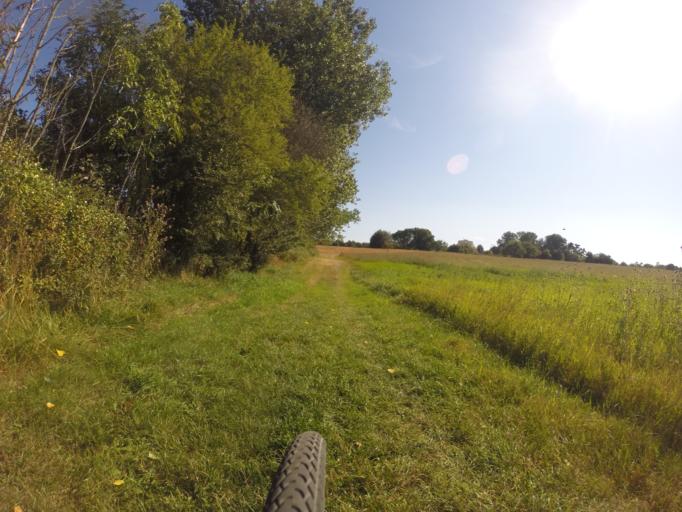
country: DK
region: Capital Region
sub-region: Herlev Kommune
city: Herlev
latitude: 55.7493
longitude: 12.4340
